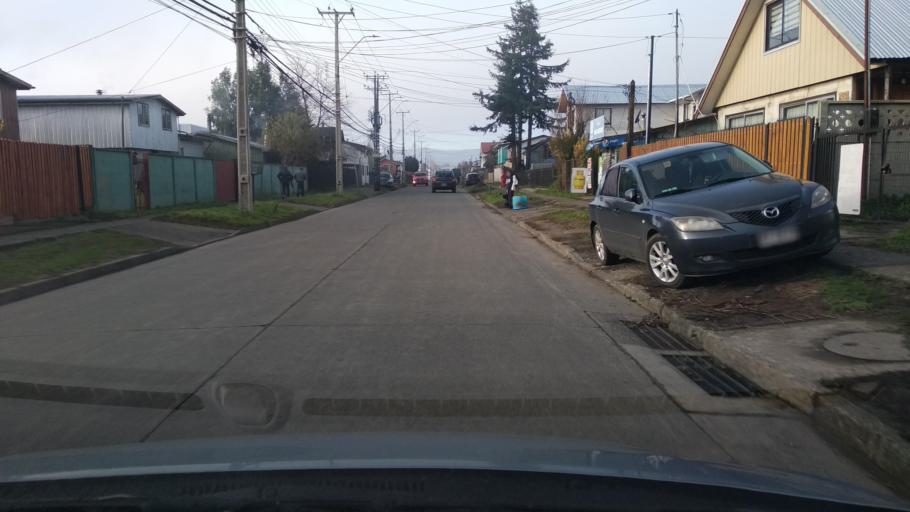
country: CL
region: Los Lagos
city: Las Animas
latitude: -39.8110
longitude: -73.2279
